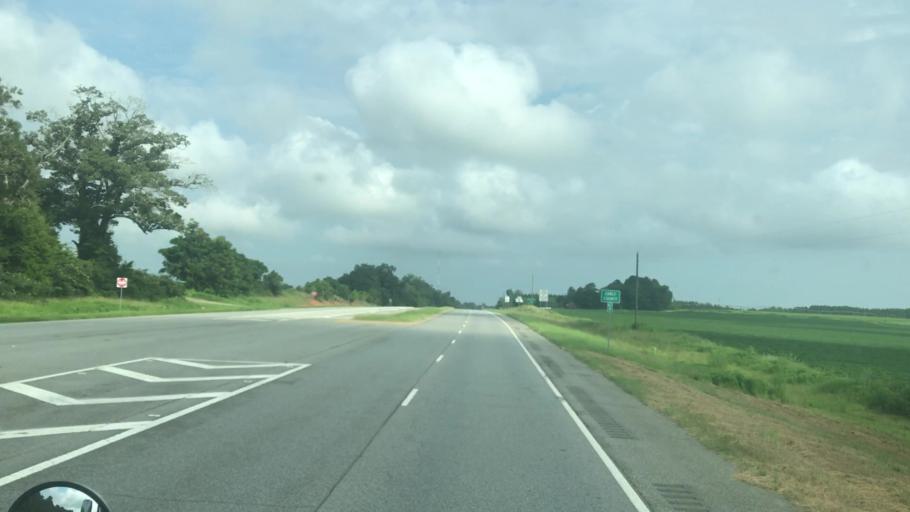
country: US
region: Georgia
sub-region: Miller County
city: Colquitt
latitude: 31.2535
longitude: -84.8023
